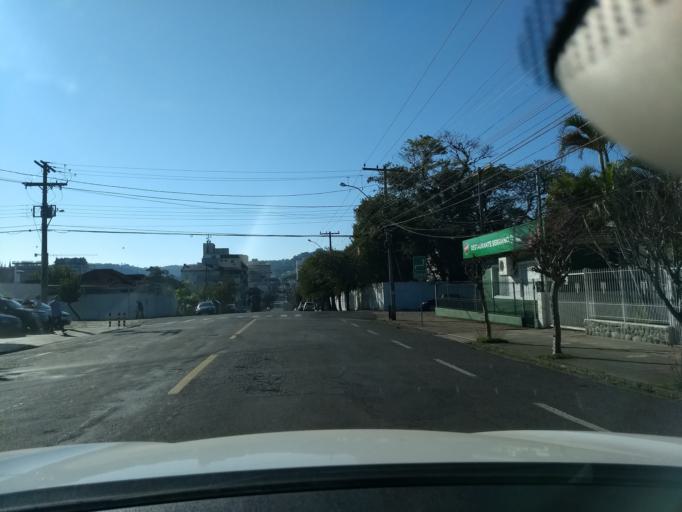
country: BR
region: Rio Grande do Sul
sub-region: Santa Cruz Do Sul
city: Santa Cruz do Sul
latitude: -29.7160
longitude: -52.4373
